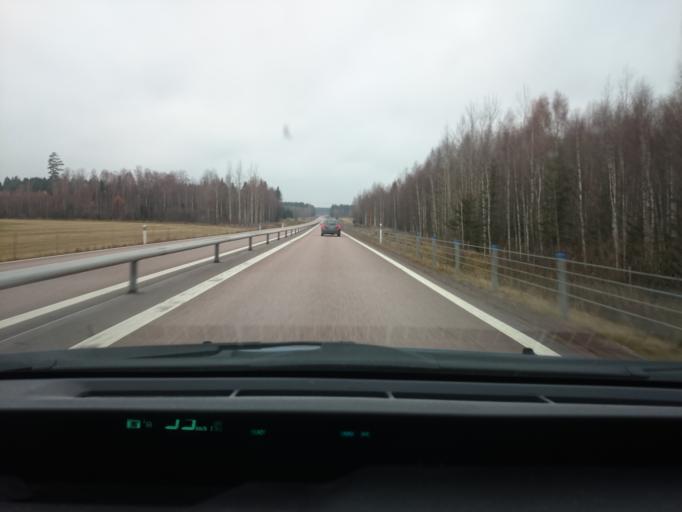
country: SE
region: Dalarna
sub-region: Avesta Kommun
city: Avesta
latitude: 60.1380
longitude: 16.2559
